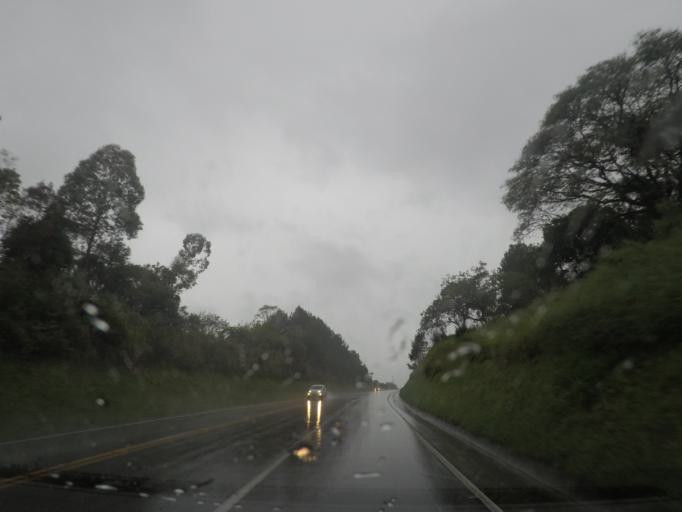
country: BR
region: Parana
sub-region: Almirante Tamandare
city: Almirante Tamandare
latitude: -25.3535
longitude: -49.3042
